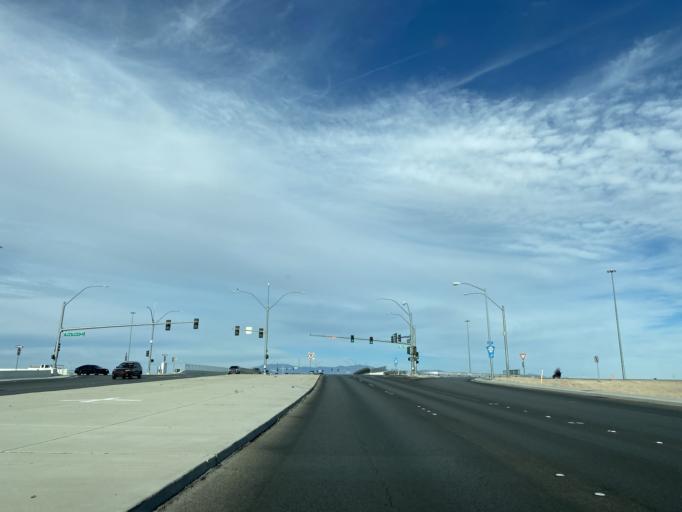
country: US
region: Nevada
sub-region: Clark County
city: Enterprise
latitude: 36.0649
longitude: -115.2245
